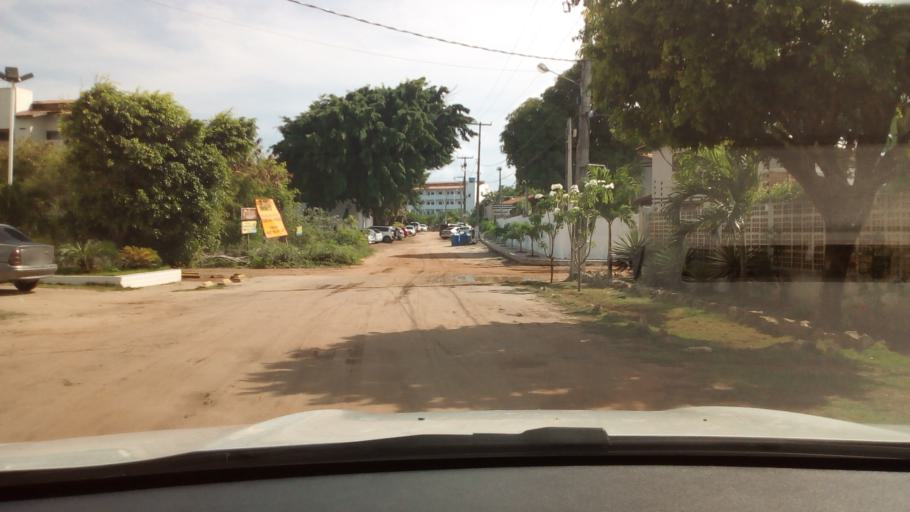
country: BR
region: Paraiba
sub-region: Conde
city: Conde
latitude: -7.3018
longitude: -34.7999
